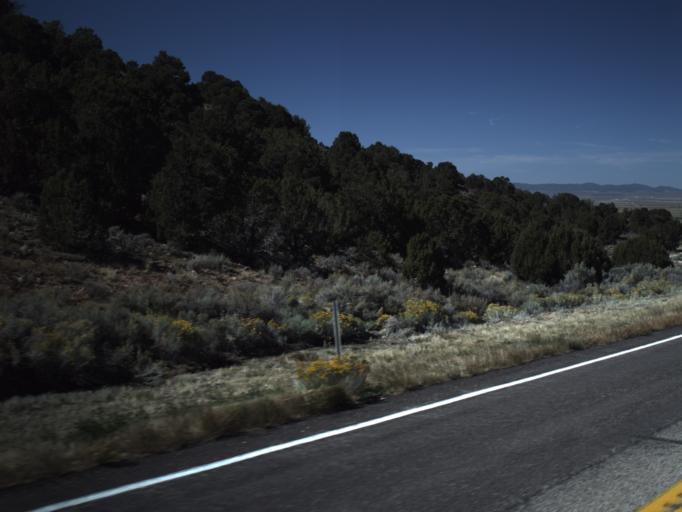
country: US
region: Utah
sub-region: Washington County
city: Enterprise
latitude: 37.6754
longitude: -113.4948
